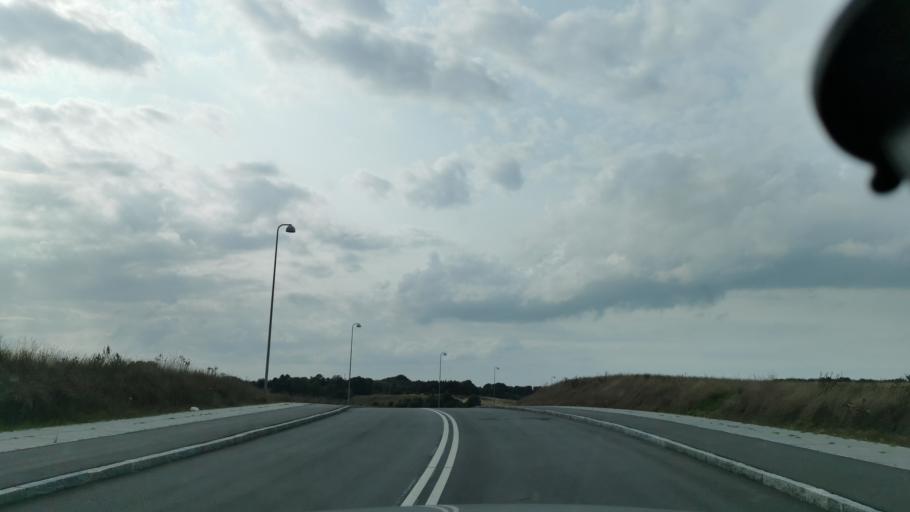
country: DK
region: Zealand
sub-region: Kalundborg Kommune
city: Kalundborg
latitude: 55.6942
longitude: 11.0807
